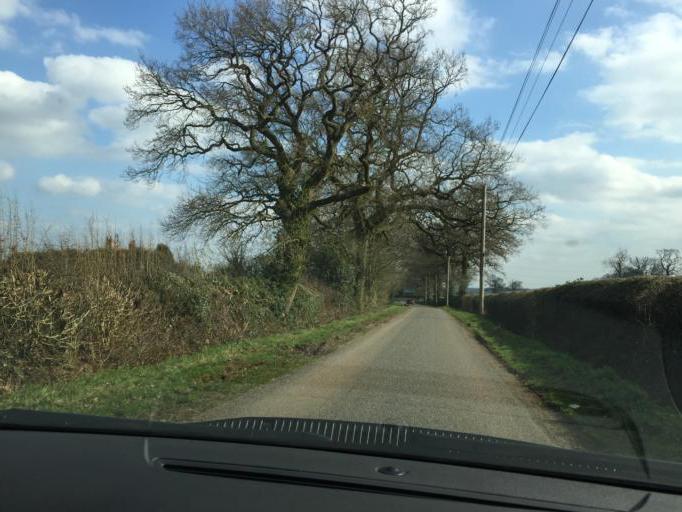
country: GB
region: England
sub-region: Coventry
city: Keresley
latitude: 52.4484
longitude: -1.5852
